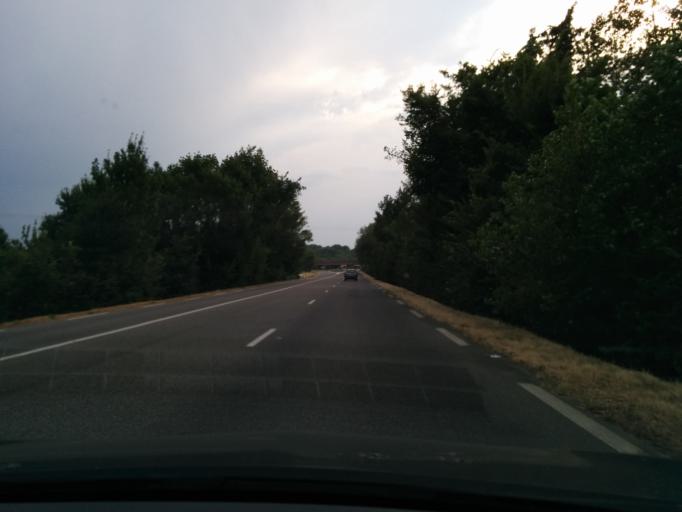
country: FR
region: Midi-Pyrenees
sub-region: Departement de la Haute-Garonne
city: Baziege
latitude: 43.4495
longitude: 1.6110
